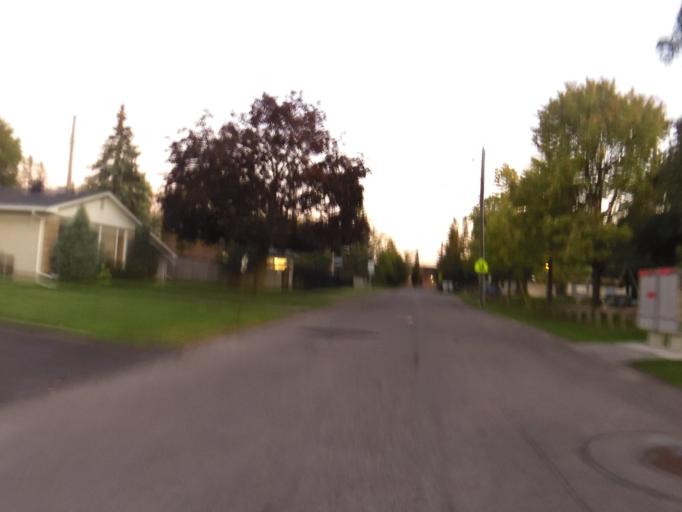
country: CA
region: Ontario
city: Ottawa
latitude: 45.3695
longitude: -75.6571
